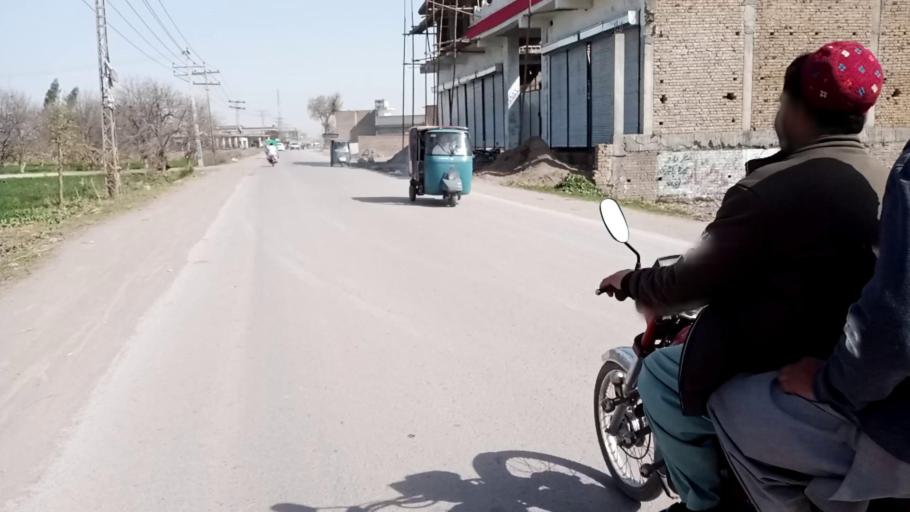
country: PK
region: Khyber Pakhtunkhwa
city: Peshawar
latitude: 34.0001
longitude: 71.6362
